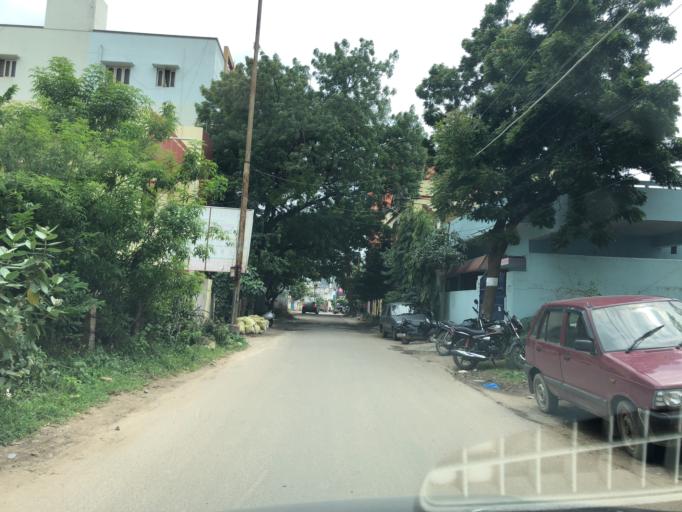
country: IN
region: Telangana
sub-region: Rangareddi
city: Quthbullapur
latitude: 17.4808
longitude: 78.4757
